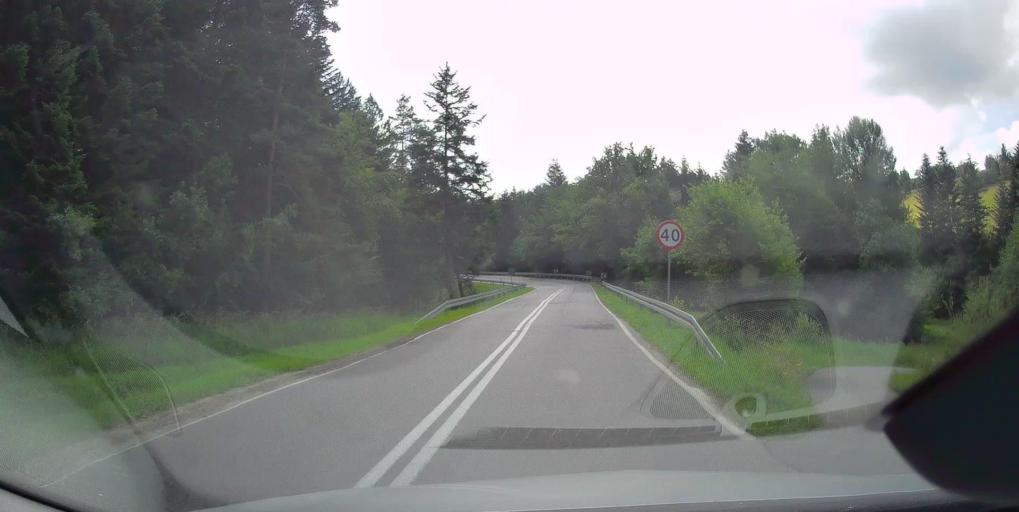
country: PL
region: Lesser Poland Voivodeship
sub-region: Powiat tarnowski
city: Zakliczyn
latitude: 49.7703
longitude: 20.7754
